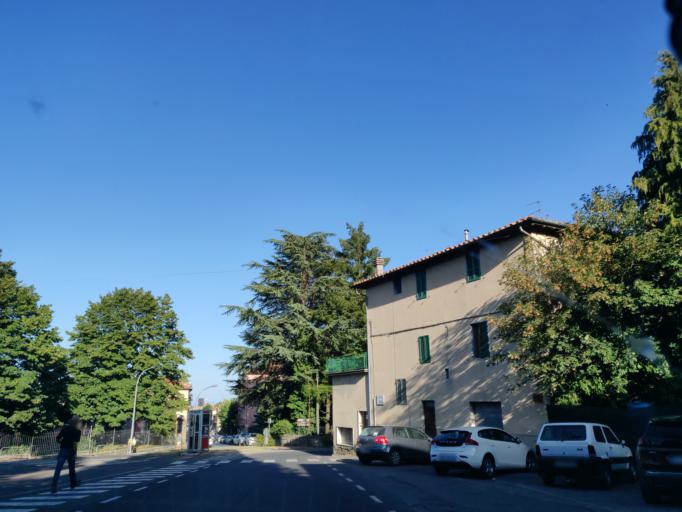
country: IT
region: Tuscany
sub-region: Provincia di Siena
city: Abbadia San Salvatore
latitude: 42.8817
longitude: 11.6734
